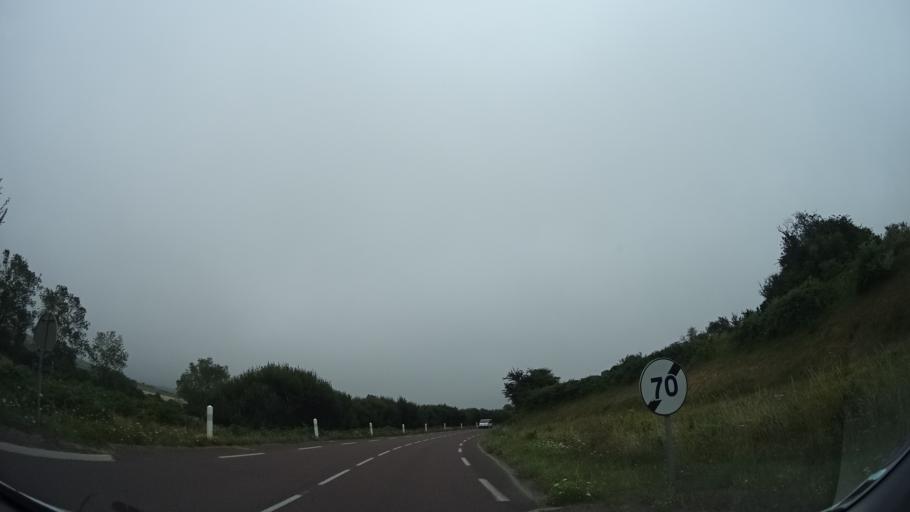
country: FR
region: Lower Normandy
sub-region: Departement de la Manche
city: Flamanville
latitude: 49.5473
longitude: -1.8473
